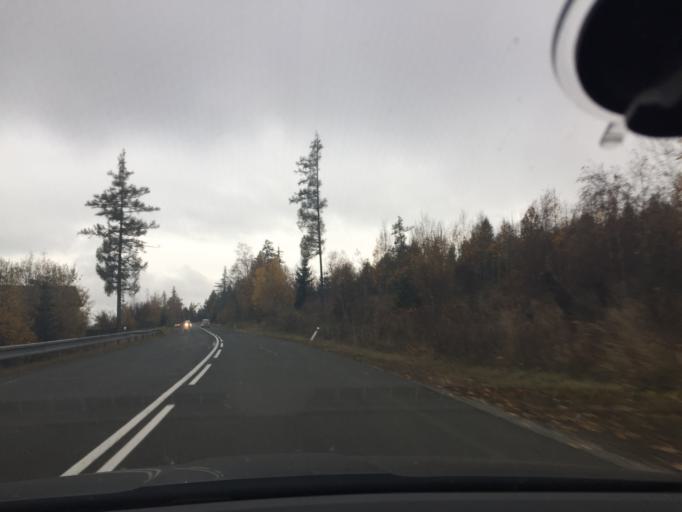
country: SK
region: Presovsky
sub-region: Okres Poprad
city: Svit
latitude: 49.1203
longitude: 20.1693
